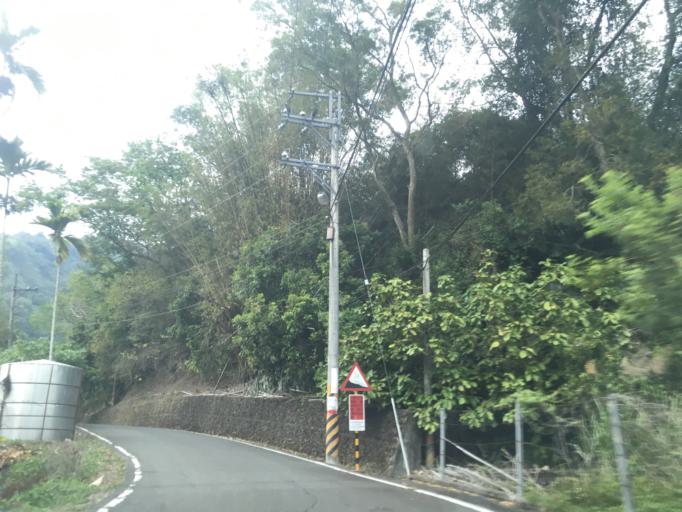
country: TW
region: Taiwan
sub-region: Nantou
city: Puli
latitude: 23.9532
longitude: 120.8650
